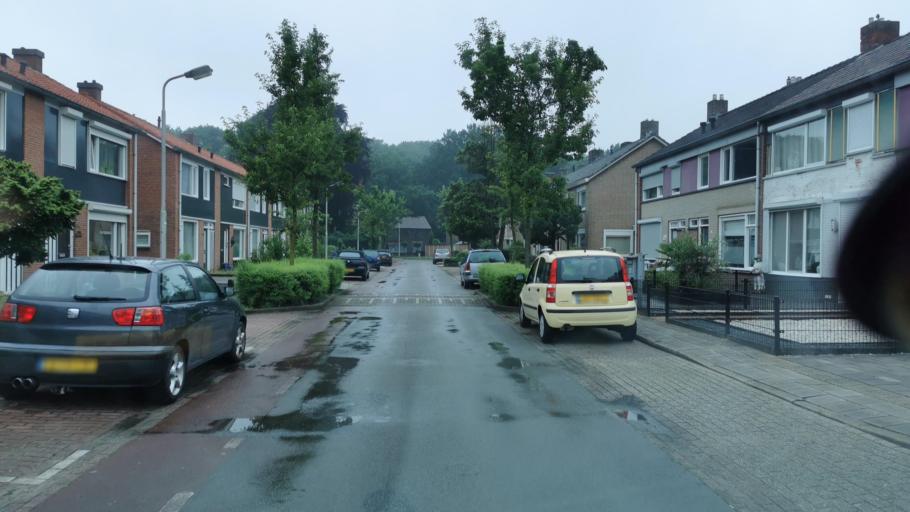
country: DE
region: North Rhine-Westphalia
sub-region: Regierungsbezirk Munster
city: Gronau
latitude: 52.2375
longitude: 7.0316
